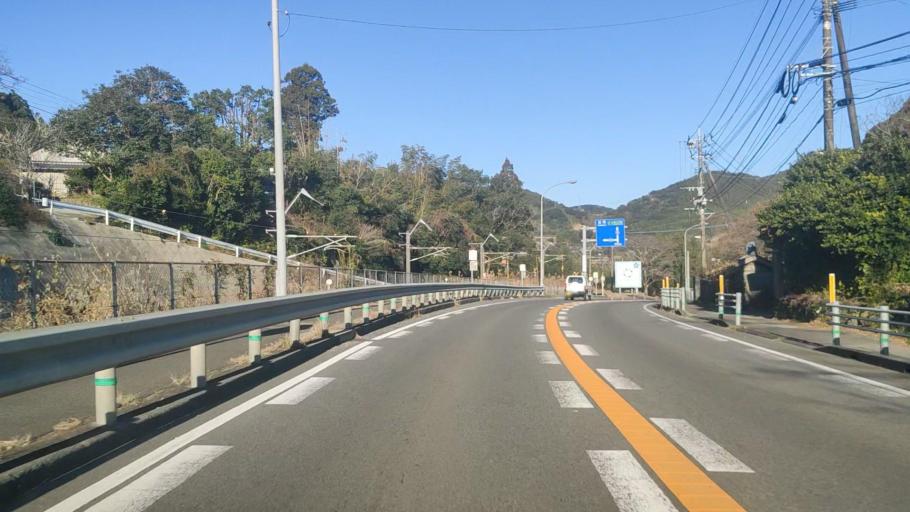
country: JP
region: Miyazaki
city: Nobeoka
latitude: 32.3771
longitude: 131.6284
